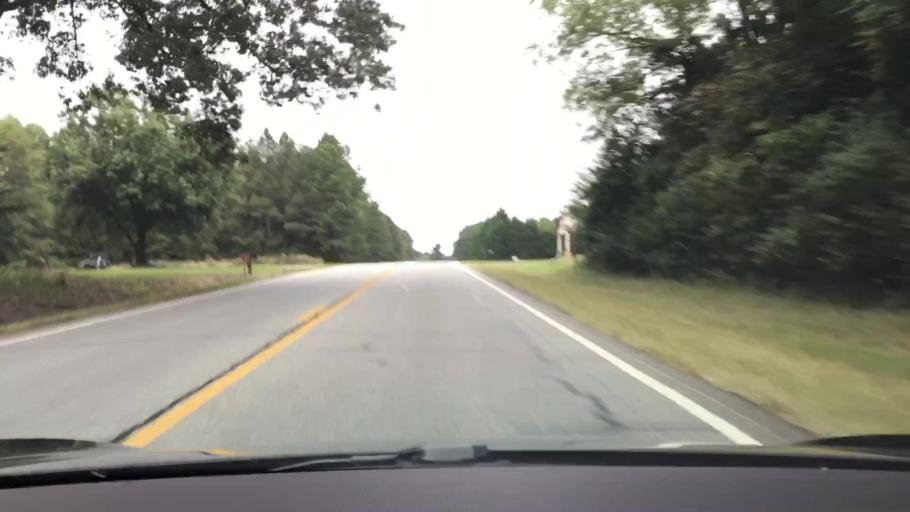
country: US
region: Georgia
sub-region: Oconee County
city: Watkinsville
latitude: 33.7742
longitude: -83.3107
